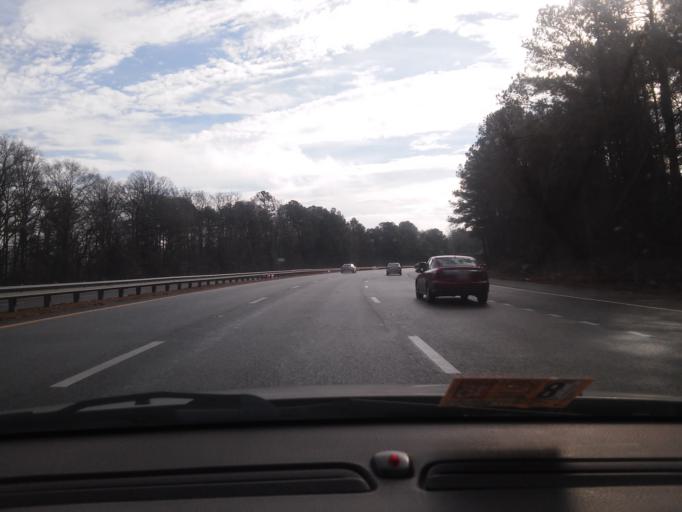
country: US
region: Virginia
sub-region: Henrico County
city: Dumbarton
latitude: 37.6041
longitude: -77.5029
